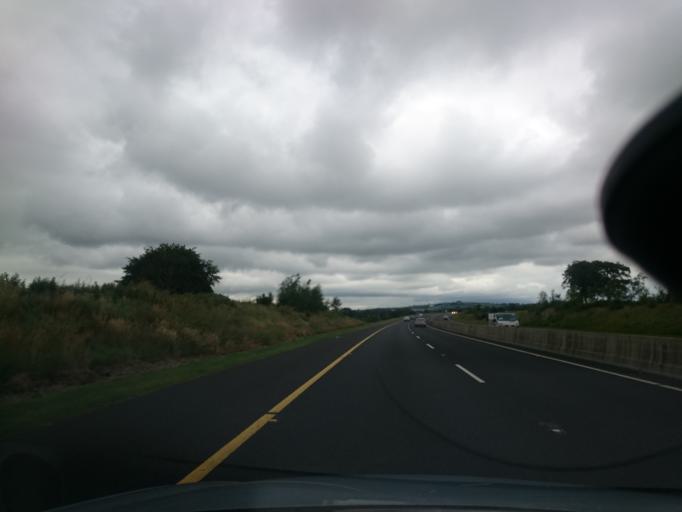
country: IE
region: Leinster
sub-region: Kildare
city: Moone
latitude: 53.0290
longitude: -6.8140
